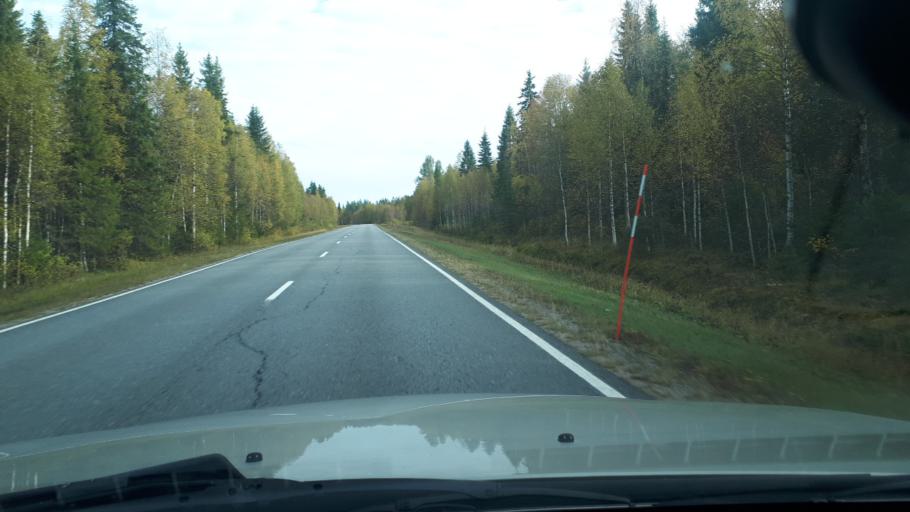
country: FI
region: Lapland
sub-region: Rovaniemi
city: Rovaniemi
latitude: 65.9572
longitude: 25.9374
